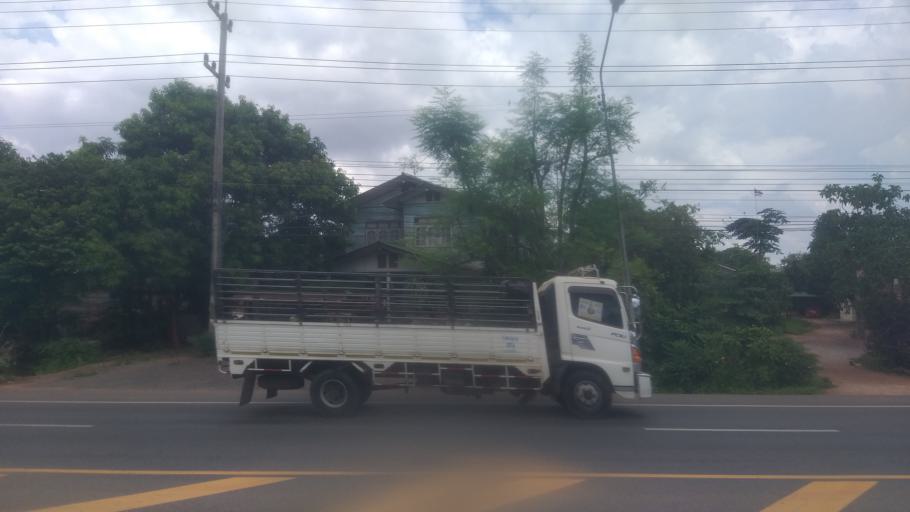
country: TH
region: Chaiyaphum
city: Noen Sa-nga
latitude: 15.6728
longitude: 101.9639
